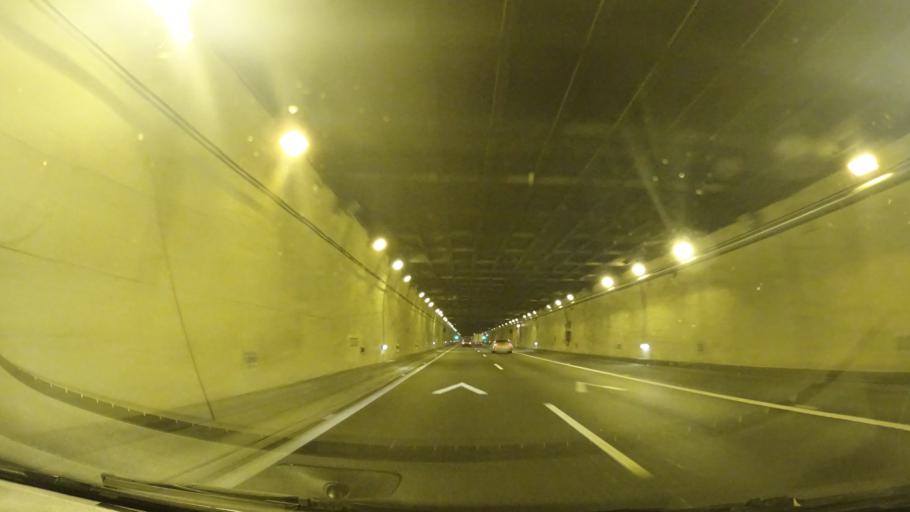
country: ES
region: Madrid
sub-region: Provincia de Madrid
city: Guadarrama
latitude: 40.7048
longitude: -4.1333
